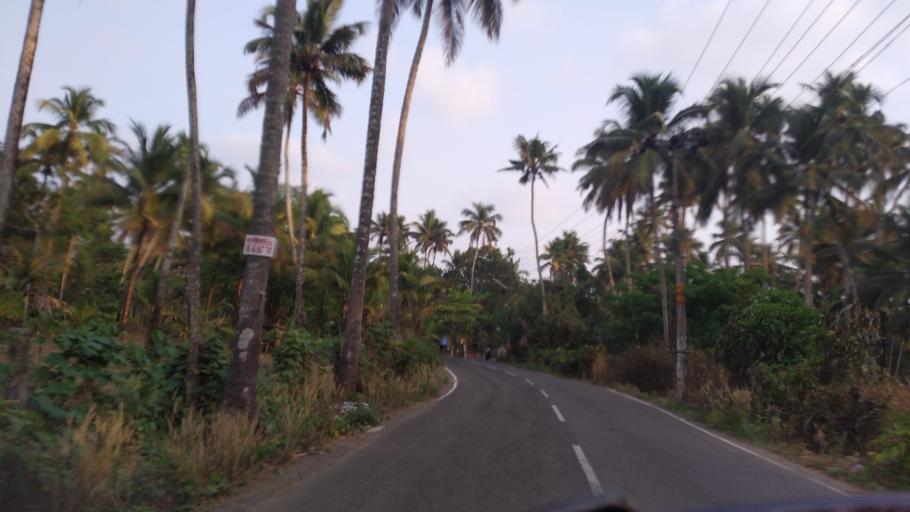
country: IN
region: Kerala
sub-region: Thrissur District
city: Thanniyam
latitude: 10.3802
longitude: 76.1013
